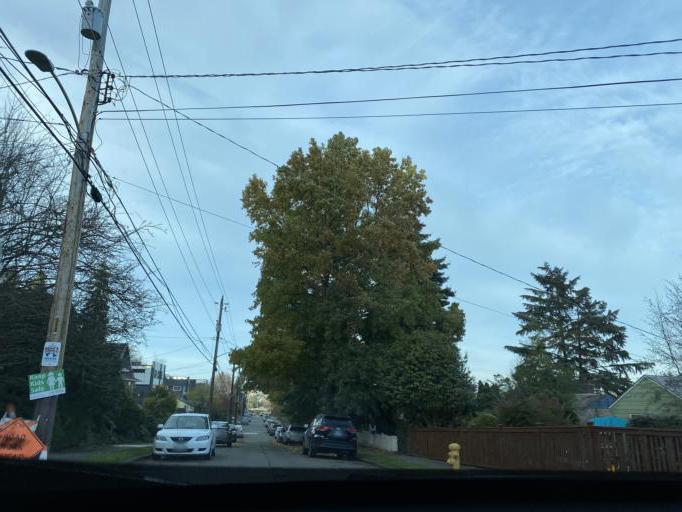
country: US
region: Washington
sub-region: King County
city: Seattle
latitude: 47.6521
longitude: -122.3860
